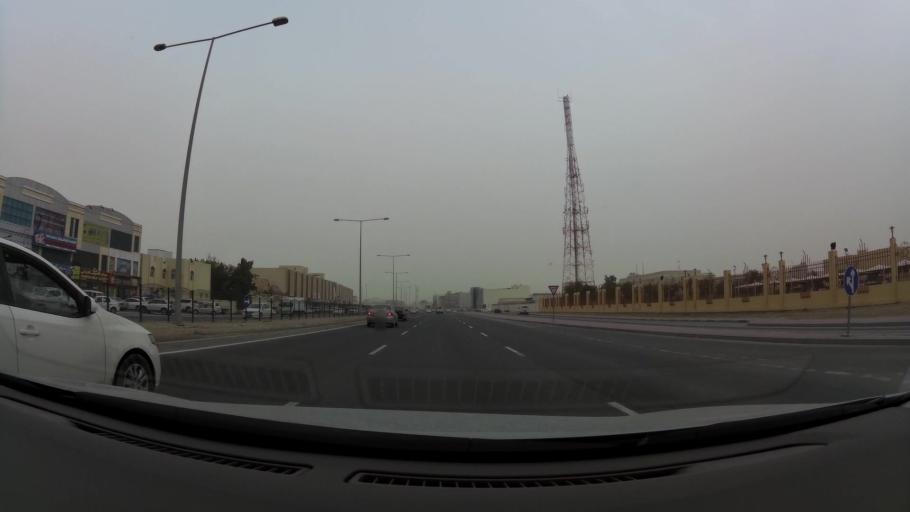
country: QA
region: Baladiyat ad Dawhah
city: Doha
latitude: 25.2320
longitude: 51.4858
